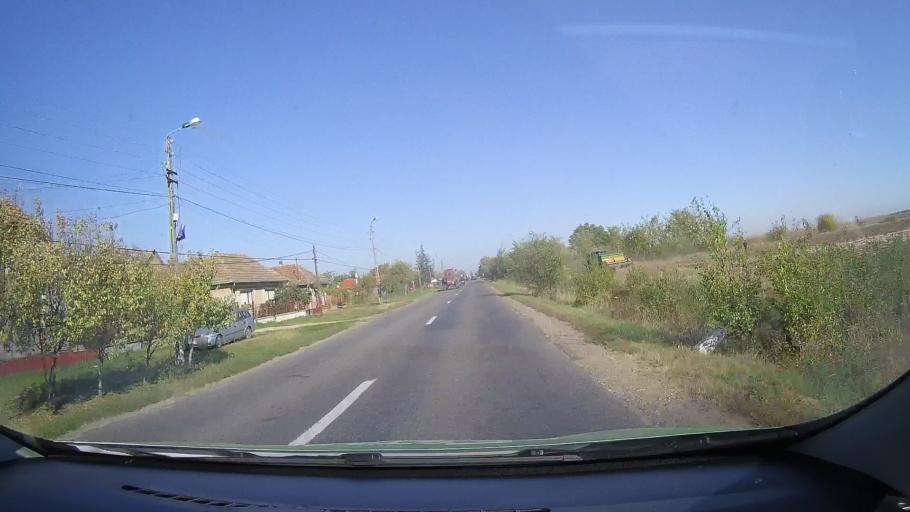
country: RO
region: Satu Mare
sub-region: Oras Tasnad
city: Tasnad
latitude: 47.5075
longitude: 22.5735
